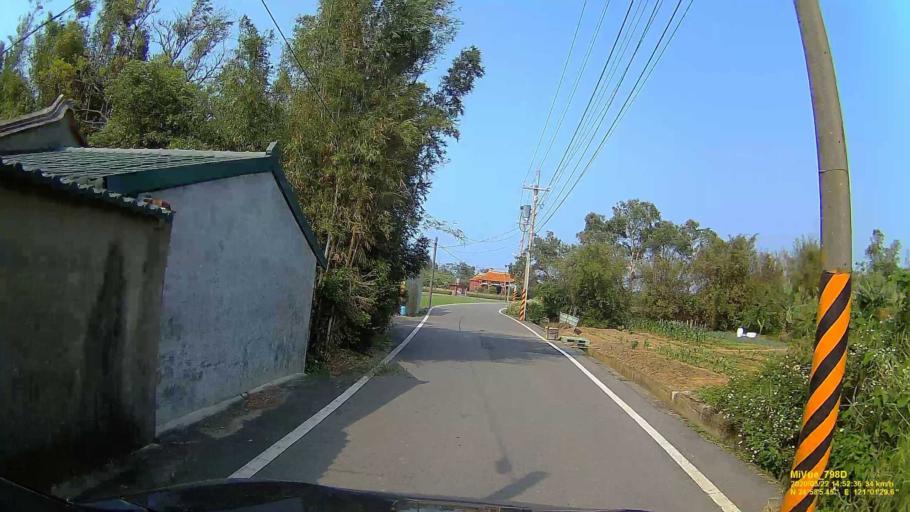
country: TW
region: Taiwan
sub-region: Hsinchu
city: Zhubei
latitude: 24.9683
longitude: 121.0250
